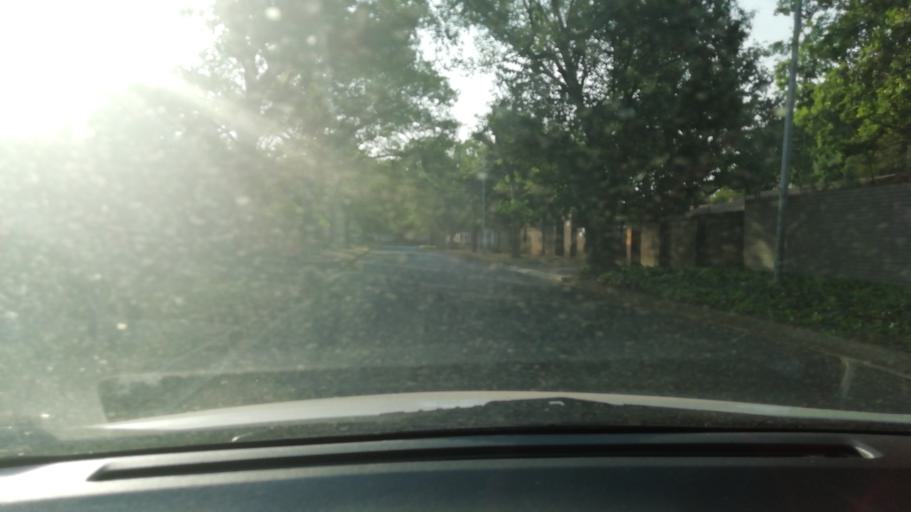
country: ZA
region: Gauteng
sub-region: Ekurhuleni Metropolitan Municipality
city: Benoni
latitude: -26.1847
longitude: 28.2889
